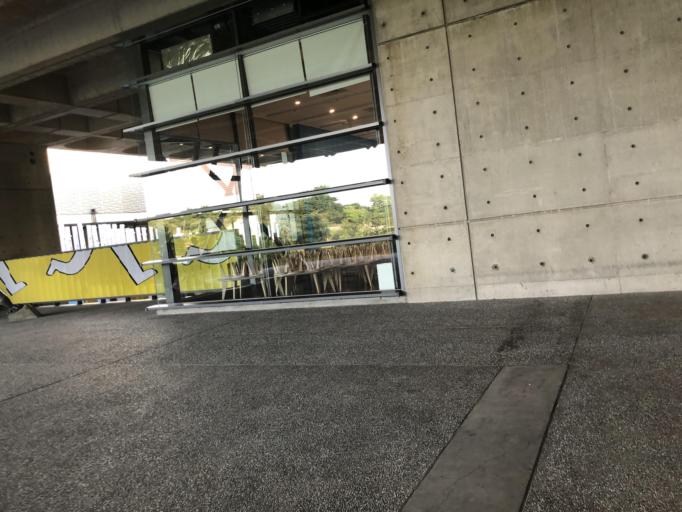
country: TW
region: Taiwan
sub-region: Tainan
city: Tainan
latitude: 23.0587
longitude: 120.2353
